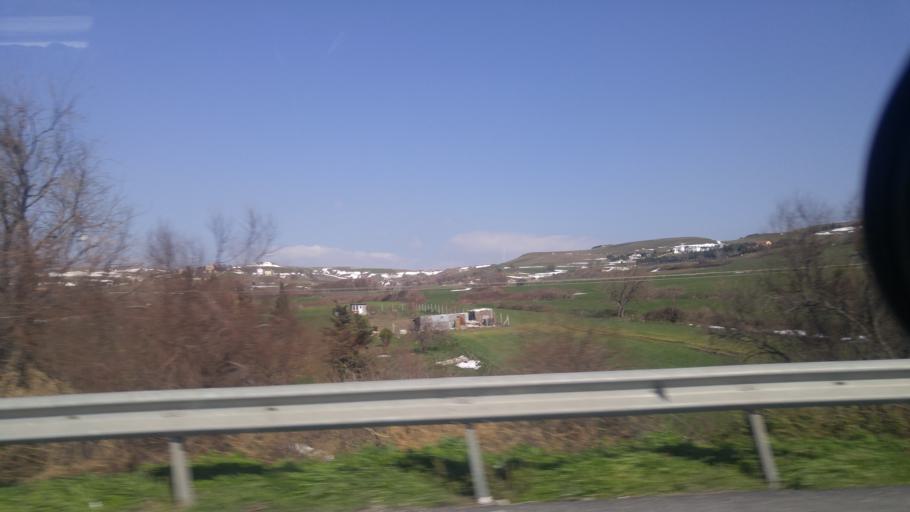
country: TR
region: Istanbul
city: Celaliye
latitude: 41.0634
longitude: 28.4063
